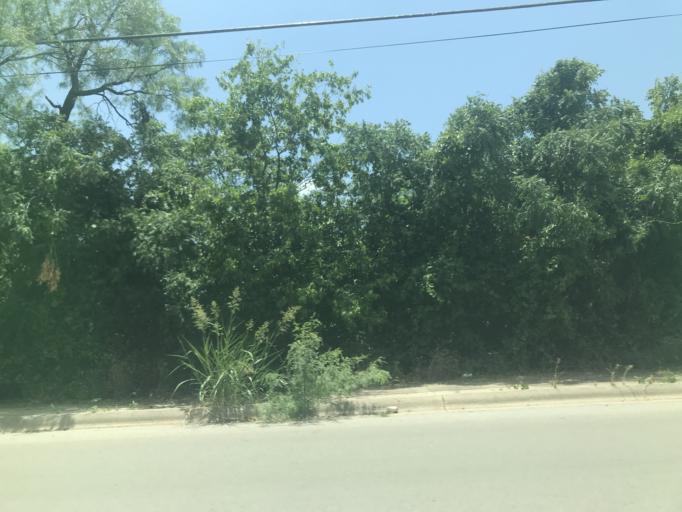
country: US
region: Texas
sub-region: Taylor County
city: Abilene
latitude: 32.4650
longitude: -99.7176
